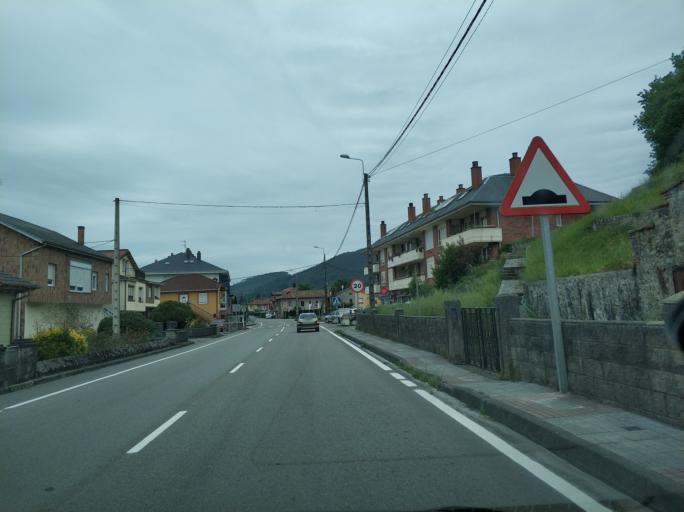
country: ES
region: Cantabria
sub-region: Provincia de Cantabria
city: Santa Maria de Cayon
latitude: 43.3183
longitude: -3.8783
